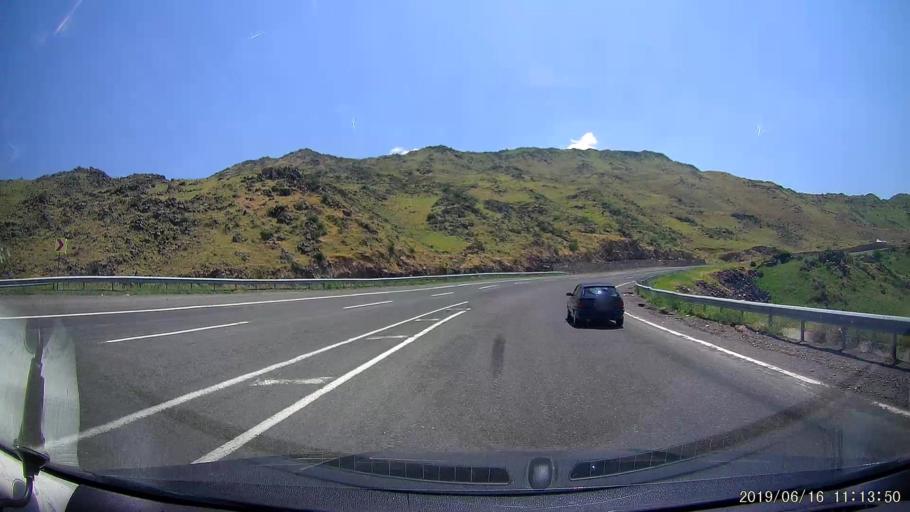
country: TR
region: Igdir
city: Igdir
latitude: 39.7866
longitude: 44.1453
